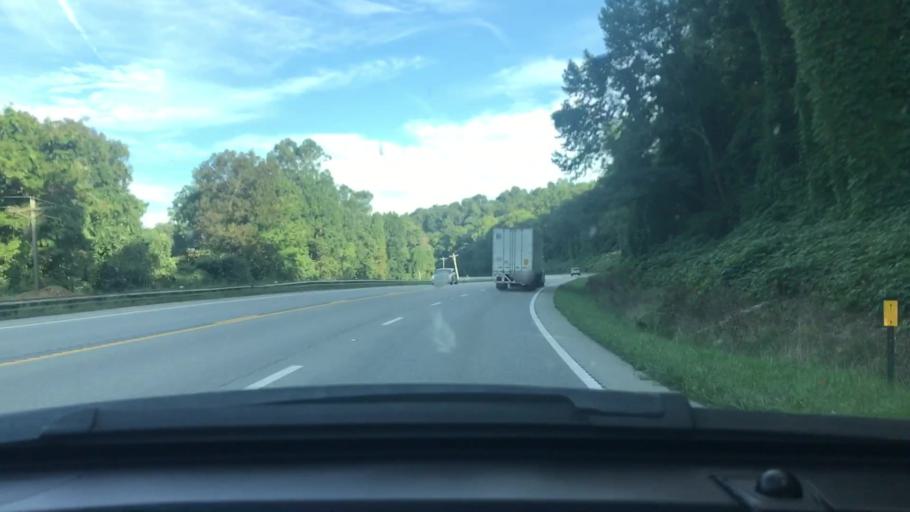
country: US
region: Arkansas
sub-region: Sharp County
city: Cherokee Village
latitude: 36.3023
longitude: -91.4127
